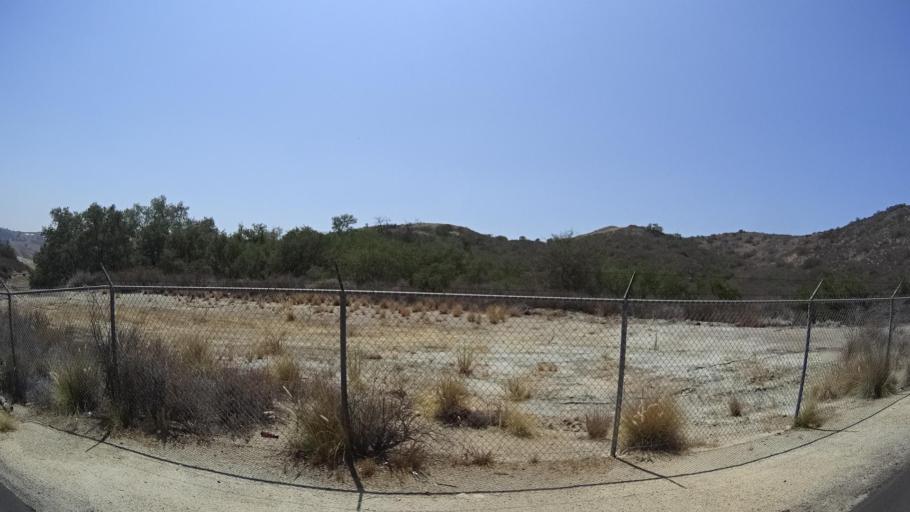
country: US
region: California
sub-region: San Diego County
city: Fallbrook
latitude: 33.4057
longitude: -117.2696
